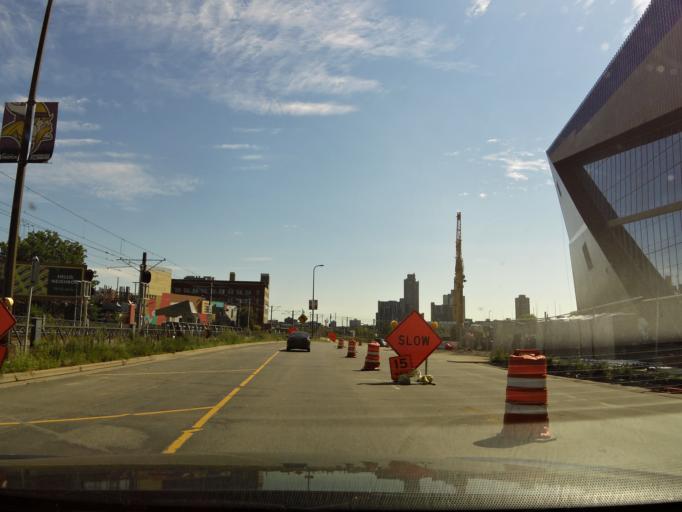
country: US
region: Minnesota
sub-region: Hennepin County
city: Minneapolis
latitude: 44.9748
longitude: -93.2567
